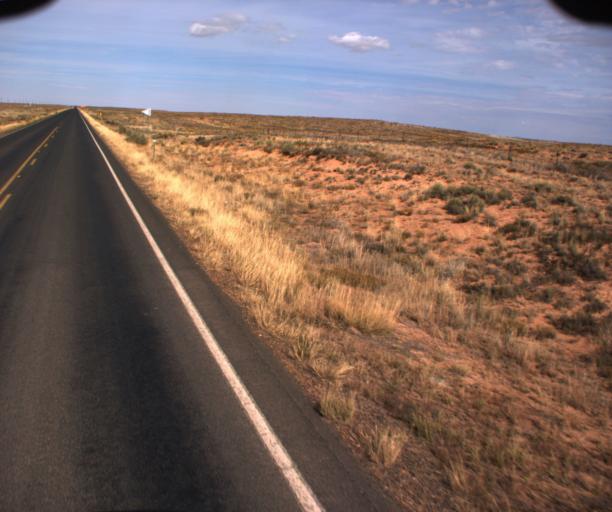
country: US
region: Arizona
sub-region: Apache County
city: Chinle
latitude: 35.9941
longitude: -109.6020
